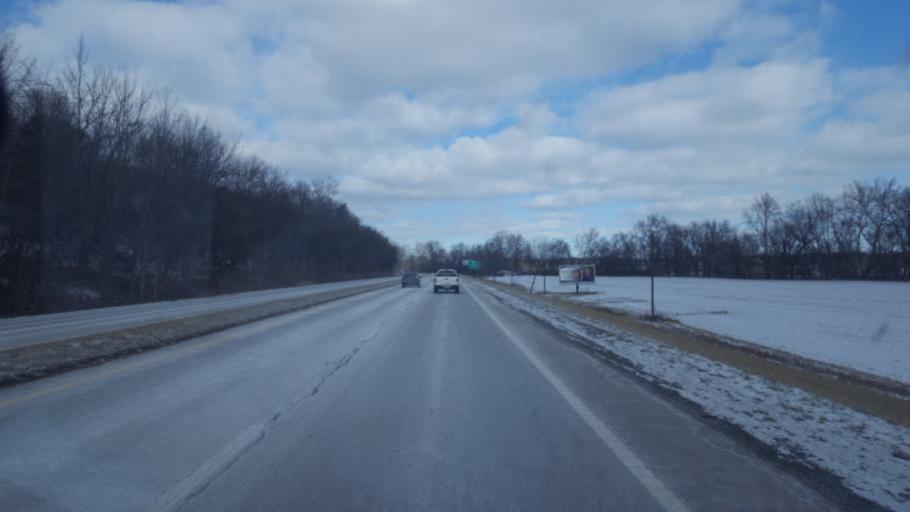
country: US
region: Ohio
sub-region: Coshocton County
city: Coshocton
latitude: 40.2568
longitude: -81.8731
